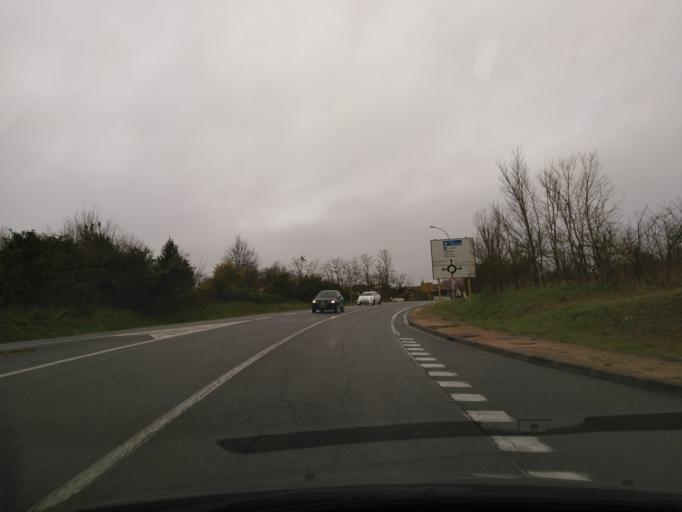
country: FR
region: Midi-Pyrenees
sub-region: Departement de la Haute-Garonne
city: Rieux-Volvestre
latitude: 43.2569
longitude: 1.1930
